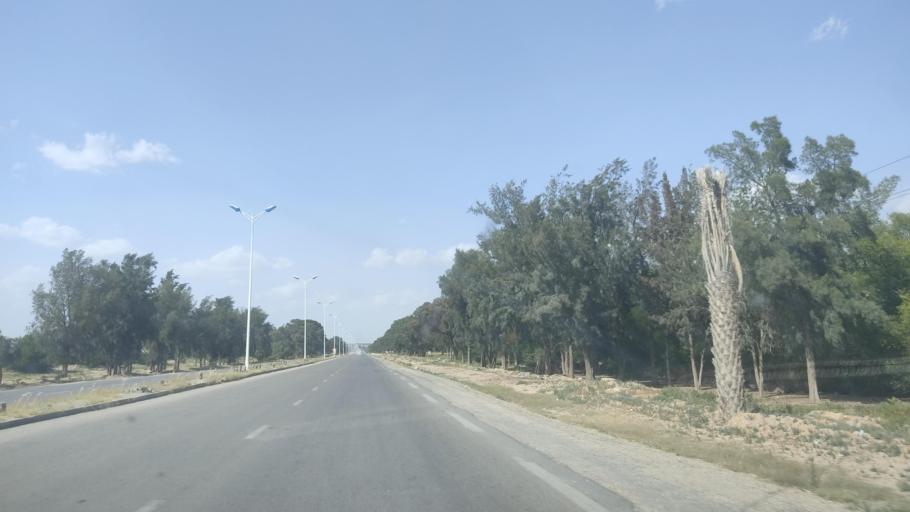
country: TN
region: Sidi Bu Zayd
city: Sidi Bouzid
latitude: 35.0654
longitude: 9.5121
